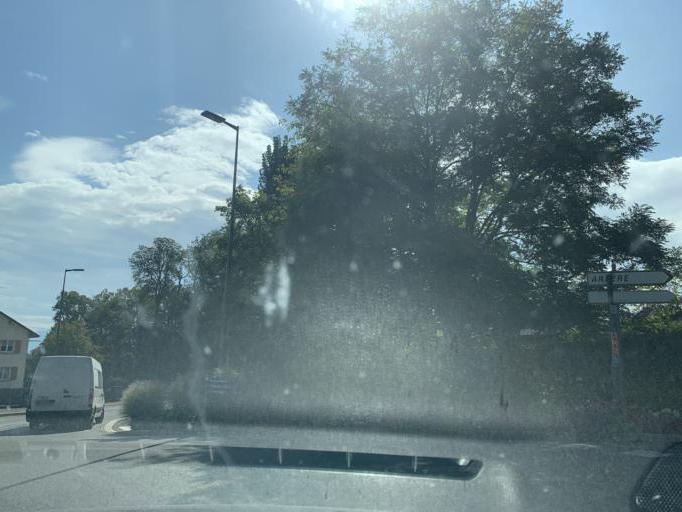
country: FR
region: Rhone-Alpes
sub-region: Departement de l'Ain
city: Divonne-les-Bains
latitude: 46.3501
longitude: 6.1319
